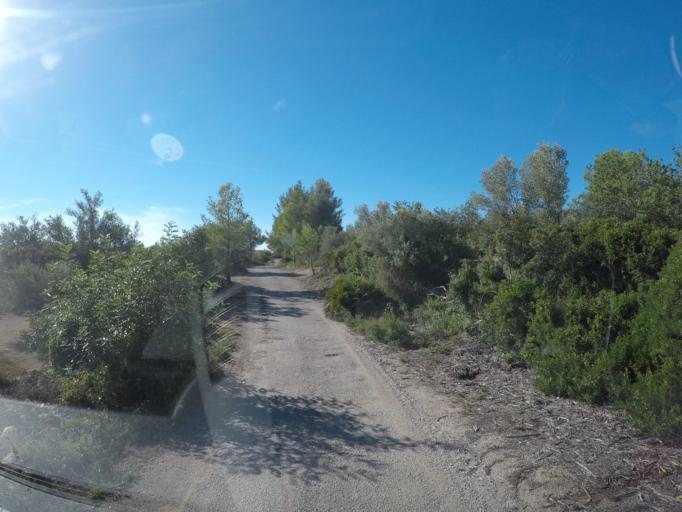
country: ES
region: Catalonia
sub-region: Provincia de Tarragona
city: El Perello
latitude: 40.9150
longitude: 0.7231
